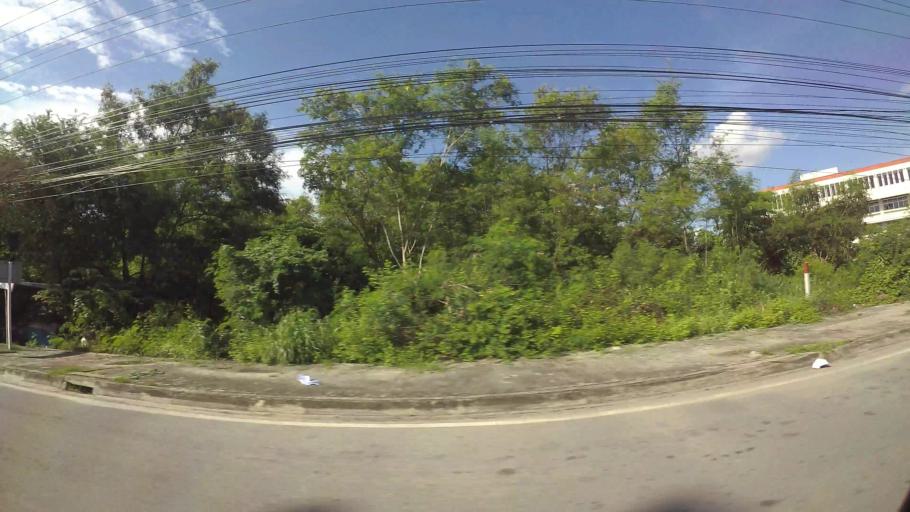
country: TH
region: Rayong
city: Rayong
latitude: 12.6682
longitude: 101.2959
